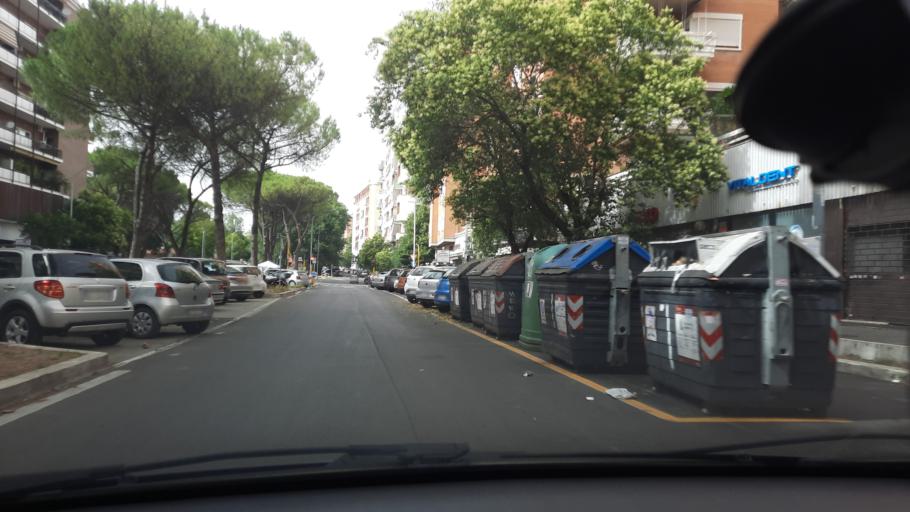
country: IT
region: Latium
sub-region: Citta metropolitana di Roma Capitale
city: Rome
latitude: 41.8556
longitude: 12.4808
